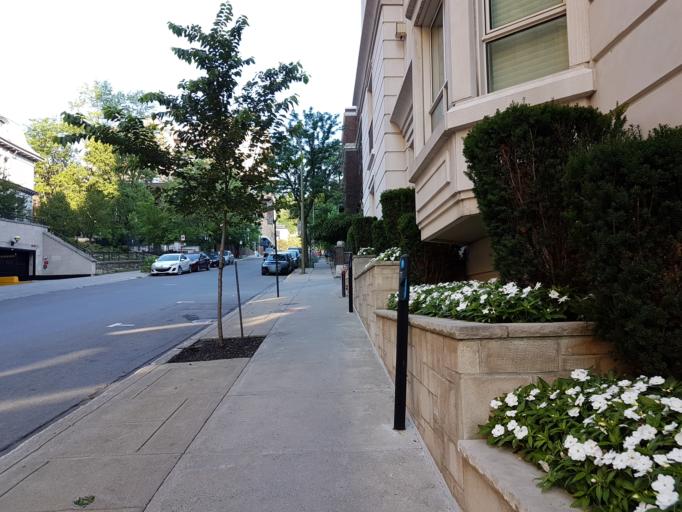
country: CA
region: Quebec
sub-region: Montreal
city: Montreal
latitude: 45.4976
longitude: -73.5817
